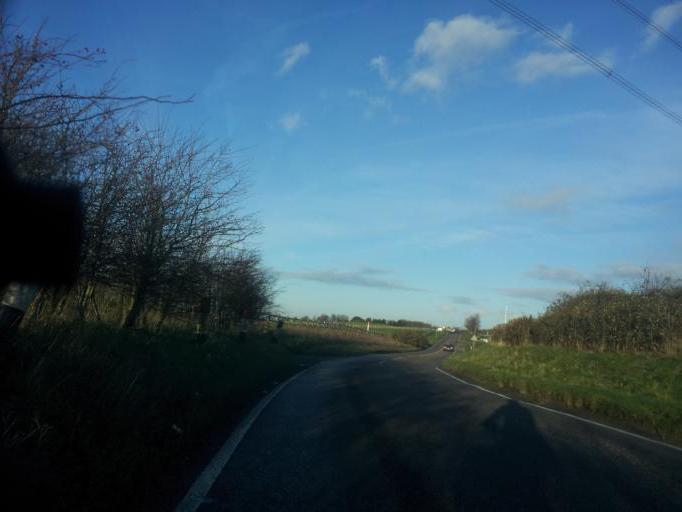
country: GB
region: England
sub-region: Kent
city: Gravesend
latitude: 51.4026
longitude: 0.3853
